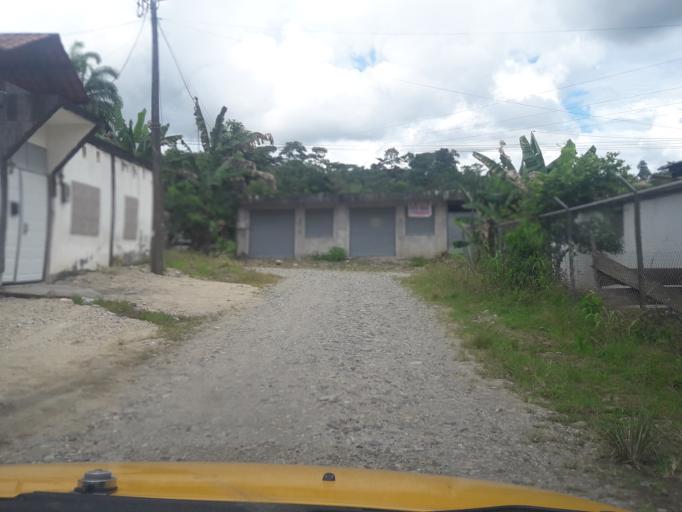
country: EC
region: Napo
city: Tena
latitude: -1.0087
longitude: -77.8114
